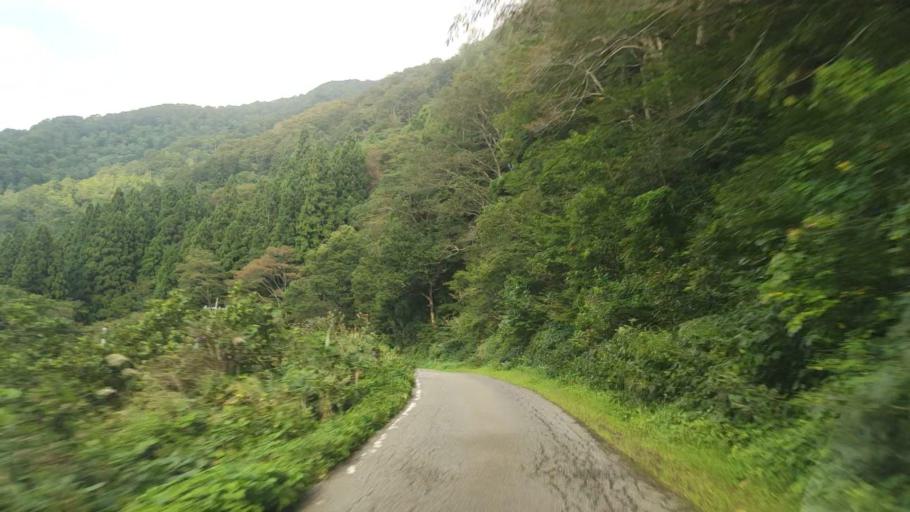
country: JP
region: Toyama
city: Yatsuomachi-higashikumisaka
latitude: 36.4419
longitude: 137.0831
